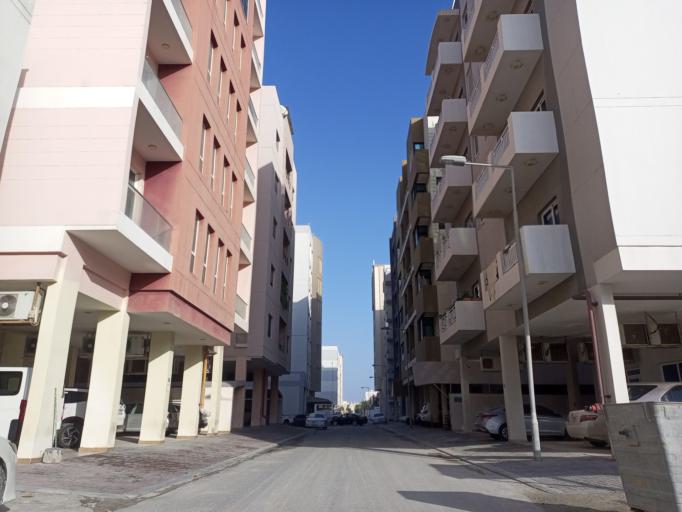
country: BH
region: Muharraq
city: Al Hadd
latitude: 26.2313
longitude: 50.6452
